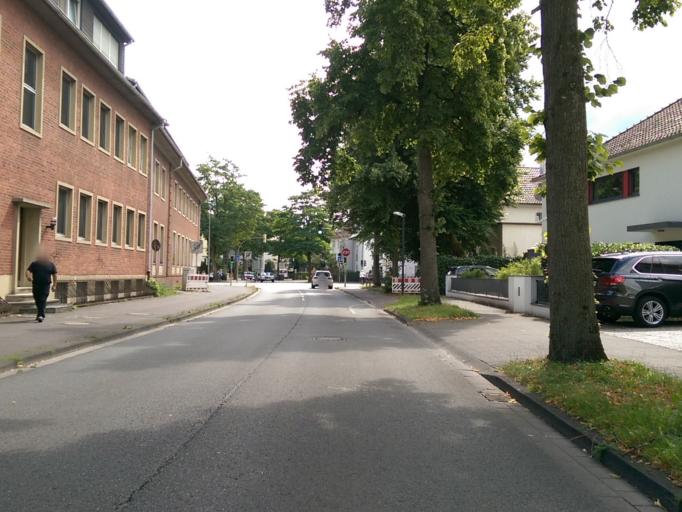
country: DE
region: North Rhine-Westphalia
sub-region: Regierungsbezirk Detmold
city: Guetersloh
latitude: 51.9114
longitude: 8.3756
